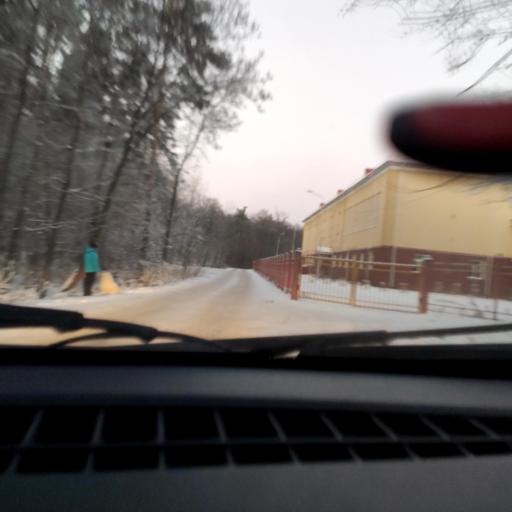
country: RU
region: Bashkortostan
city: Ufa
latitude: 54.7553
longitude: 55.9833
